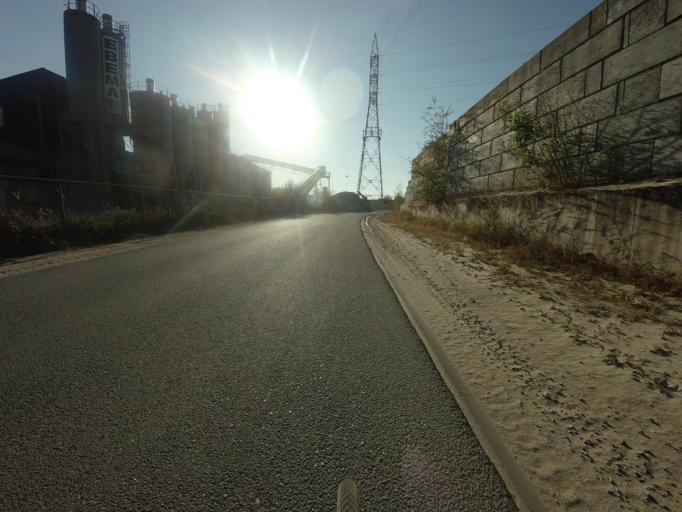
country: BE
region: Flanders
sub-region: Provincie Antwerpen
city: Rijkevorsel
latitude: 51.3303
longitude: 4.7446
